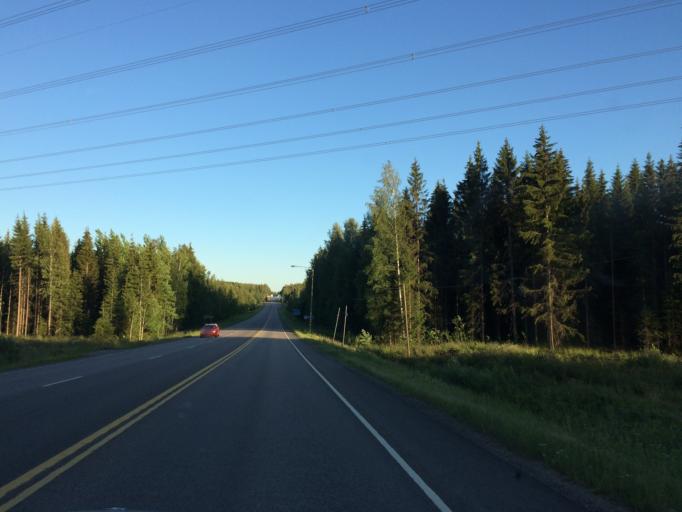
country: FI
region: Haeme
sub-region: Riihimaeki
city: Riihimaeki
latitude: 60.7564
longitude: 24.7195
